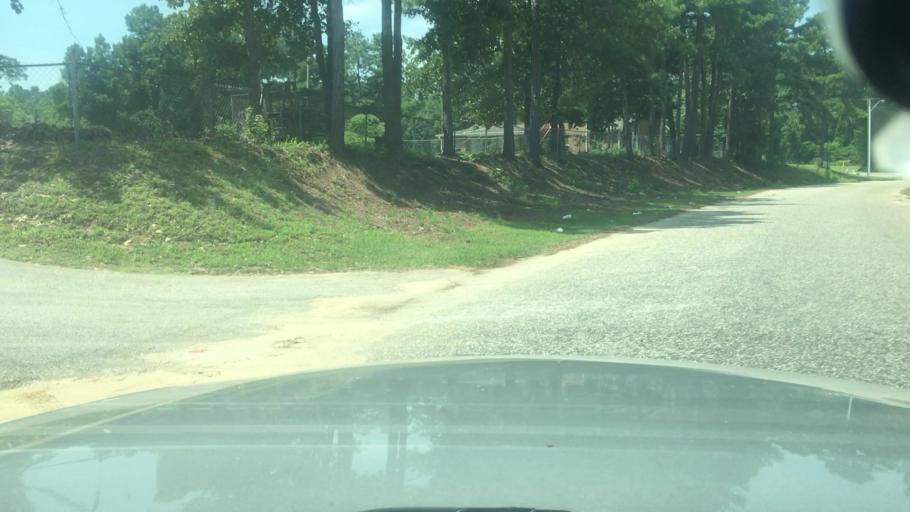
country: US
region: North Carolina
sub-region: Hoke County
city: Rockfish
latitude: 35.0393
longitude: -78.9961
